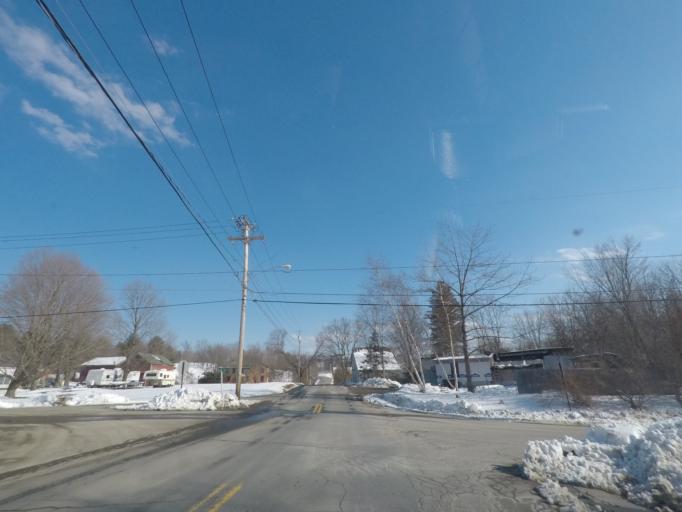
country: US
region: New York
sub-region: Saratoga County
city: Stillwater
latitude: 42.9058
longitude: -73.5107
